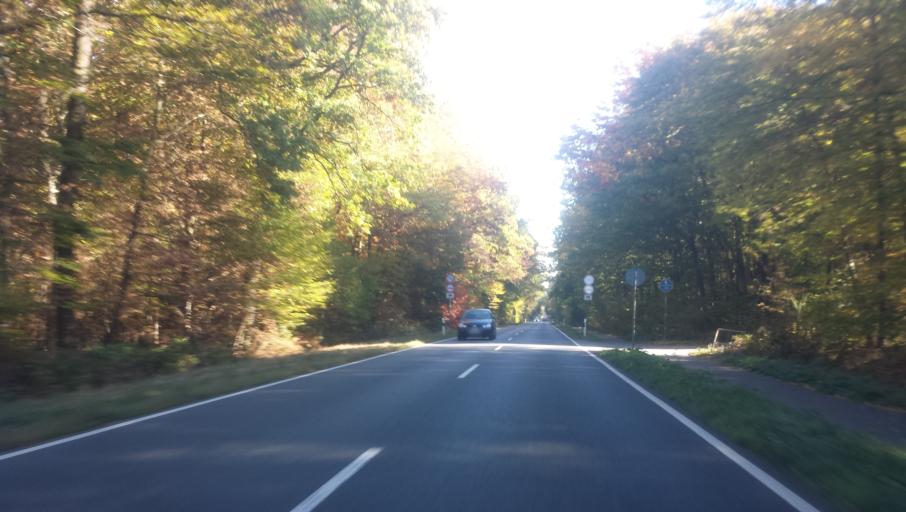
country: DE
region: Hesse
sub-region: Regierungsbezirk Darmstadt
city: Messel
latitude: 49.8994
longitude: 8.7241
